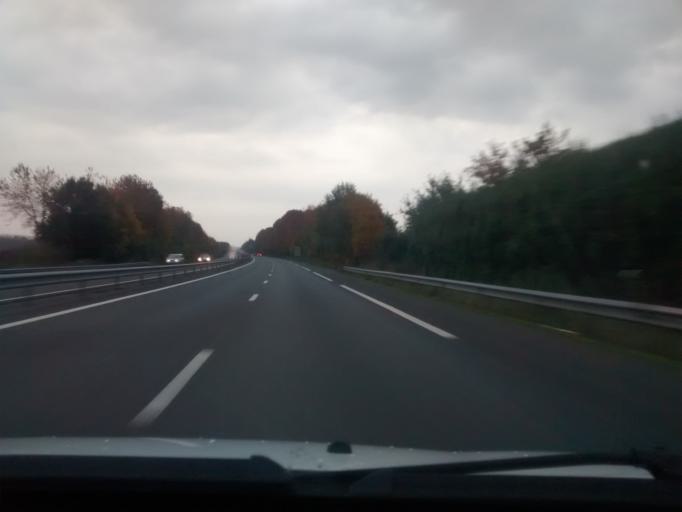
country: FR
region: Brittany
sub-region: Departement d'Ille-et-Vilaine
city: Tinteniac
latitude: 48.3318
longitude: -1.8578
